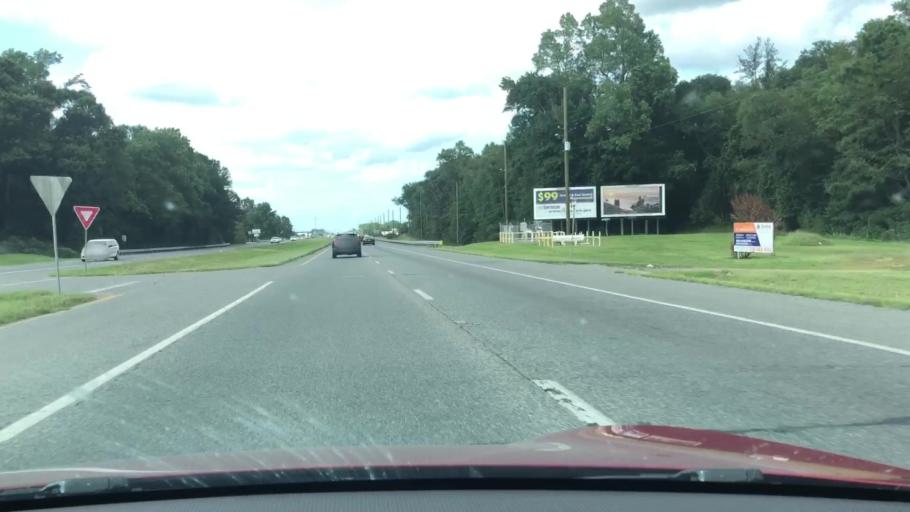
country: US
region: Delaware
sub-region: Sussex County
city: Seaford
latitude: 38.6778
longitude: -75.5917
